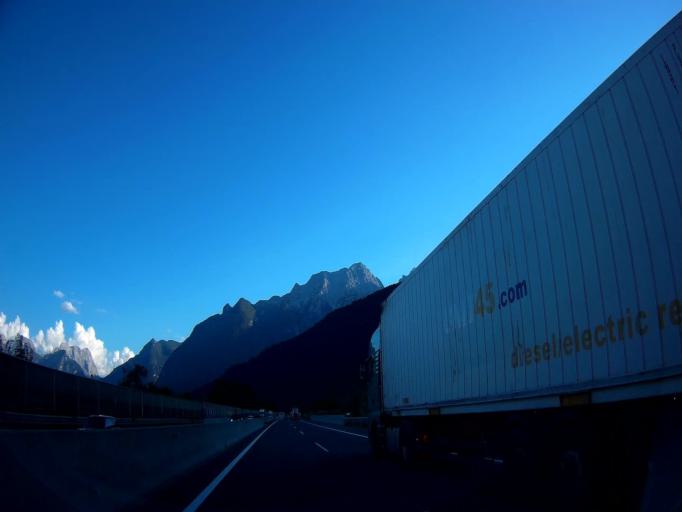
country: AT
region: Salzburg
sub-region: Politischer Bezirk Hallein
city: Kuchl
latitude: 47.6414
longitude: 13.1322
